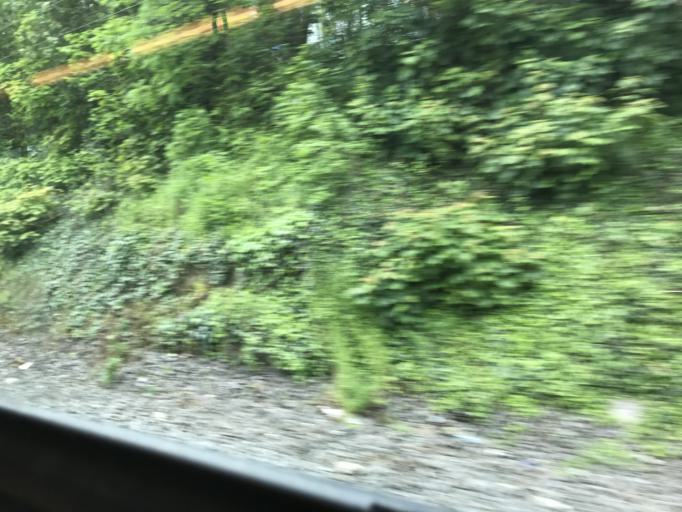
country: IE
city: Donnycarney
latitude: 53.3713
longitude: -6.2115
